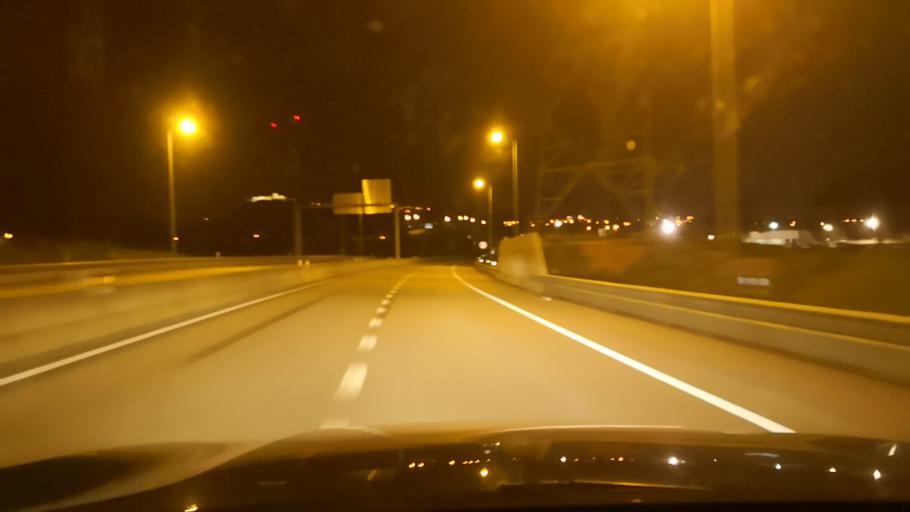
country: PT
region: Setubal
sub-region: Setubal
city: Setubal
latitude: 38.5513
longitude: -8.8625
